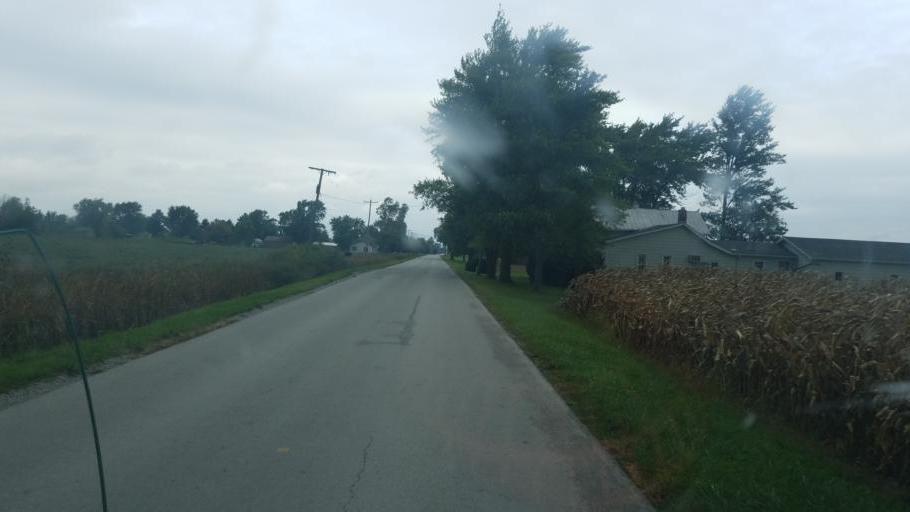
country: US
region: Ohio
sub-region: Wood County
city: North Baltimore
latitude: 41.2651
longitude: -83.6696
